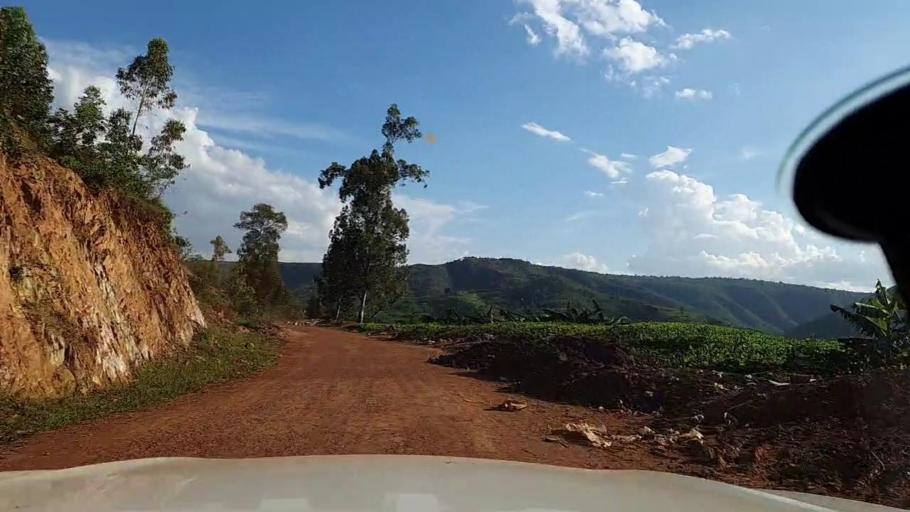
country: RW
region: Kigali
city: Kigali
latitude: -1.8695
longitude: 29.9314
